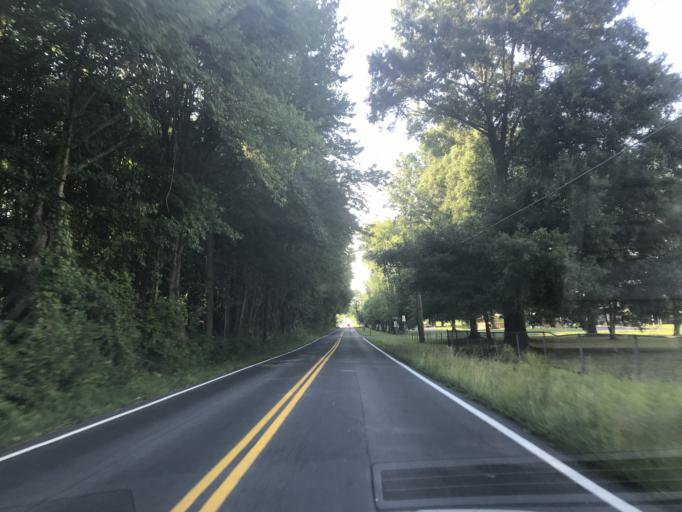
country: US
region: Maryland
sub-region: Harford County
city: Aberdeen
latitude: 39.5204
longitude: -76.1359
